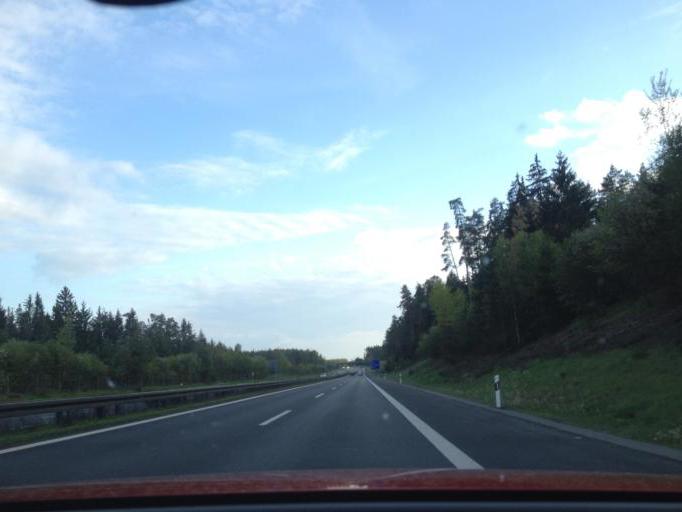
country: DE
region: Bavaria
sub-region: Upper Palatinate
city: Mitterteich
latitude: 49.9222
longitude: 12.2236
